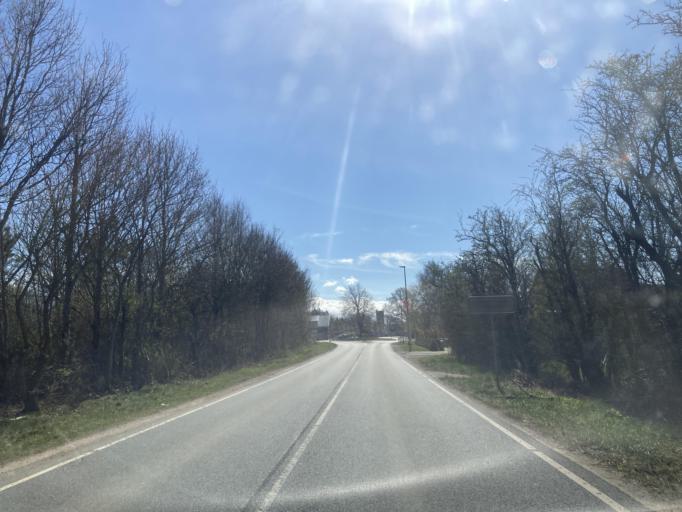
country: DK
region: Capital Region
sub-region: Gribskov Kommune
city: Graested
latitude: 56.0292
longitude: 12.2806
